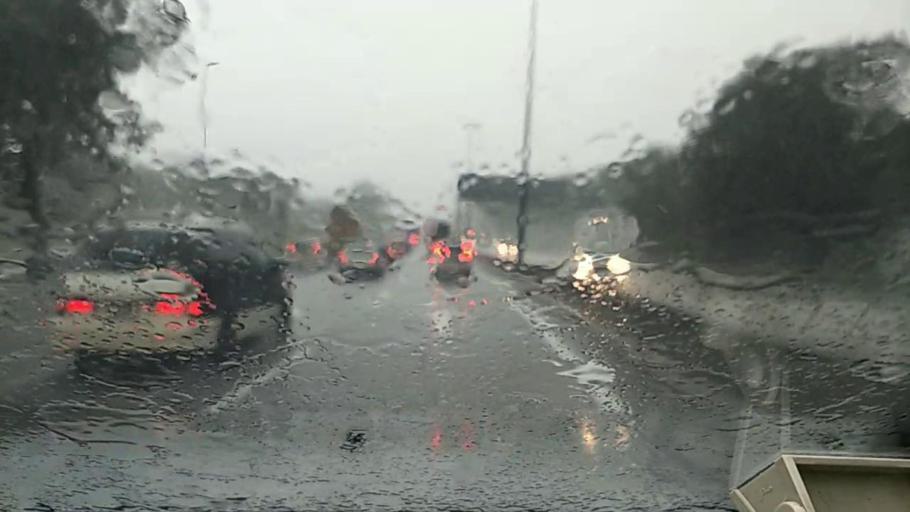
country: MY
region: Selangor
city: Kampong Baharu Balakong
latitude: 2.9804
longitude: 101.7368
